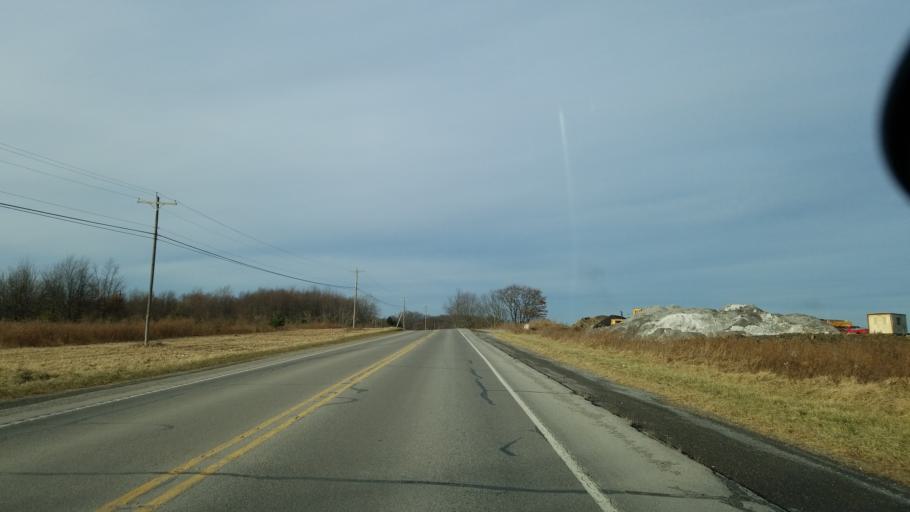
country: US
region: Pennsylvania
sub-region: Clearfield County
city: Curwensville
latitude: 41.0156
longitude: -78.6421
